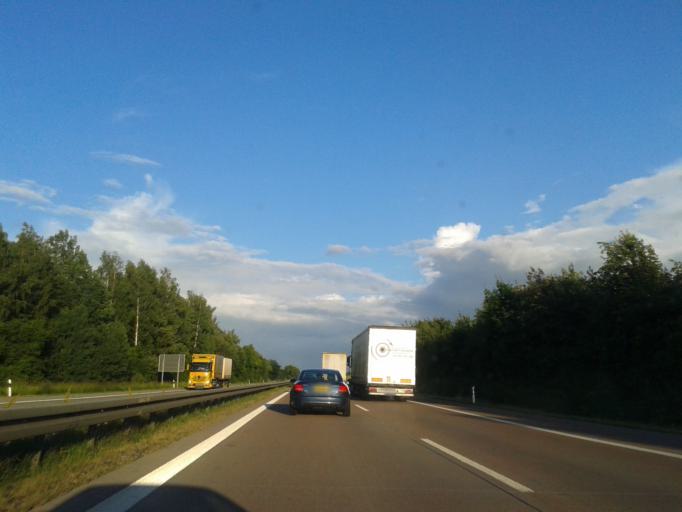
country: DE
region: Saxony
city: Ostrau
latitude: 51.2314
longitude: 12.8926
